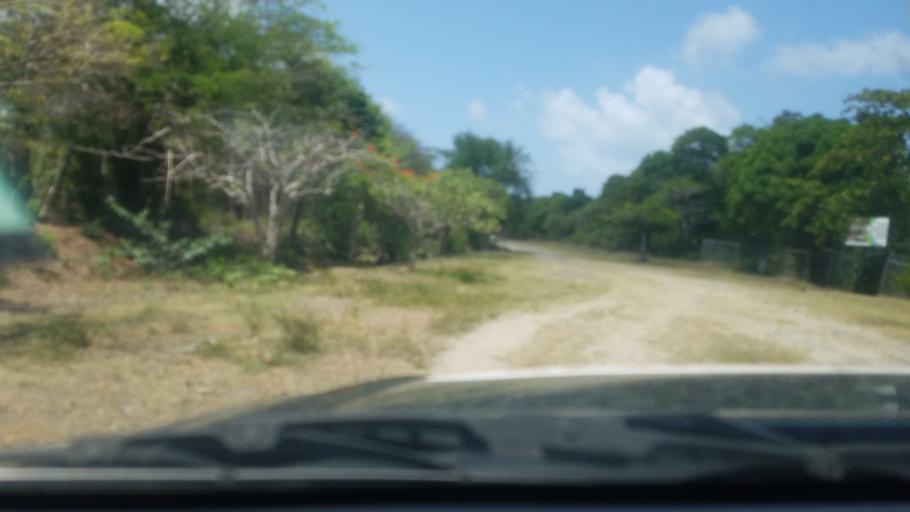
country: LC
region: Vieux-Fort
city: Vieux Fort
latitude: 13.7484
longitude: -60.9430
